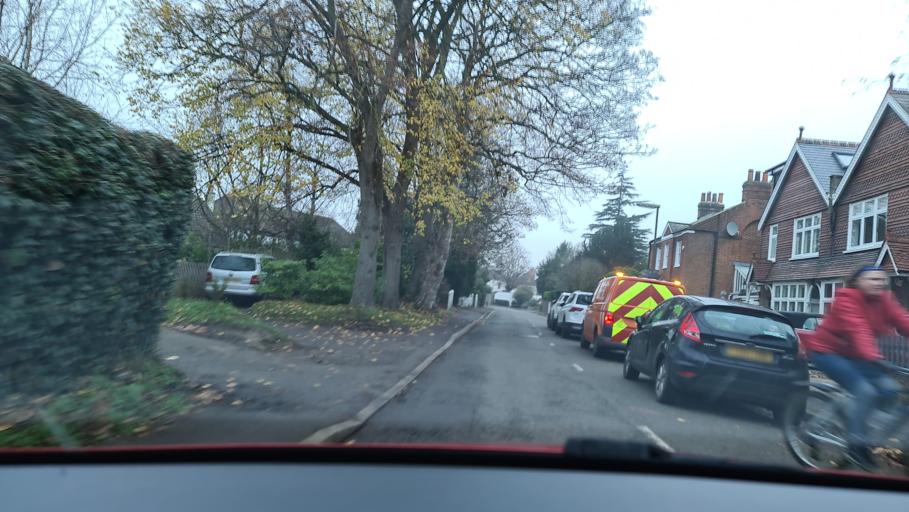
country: GB
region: England
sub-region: Surrey
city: Thames Ditton
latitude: 51.3852
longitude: -0.3292
